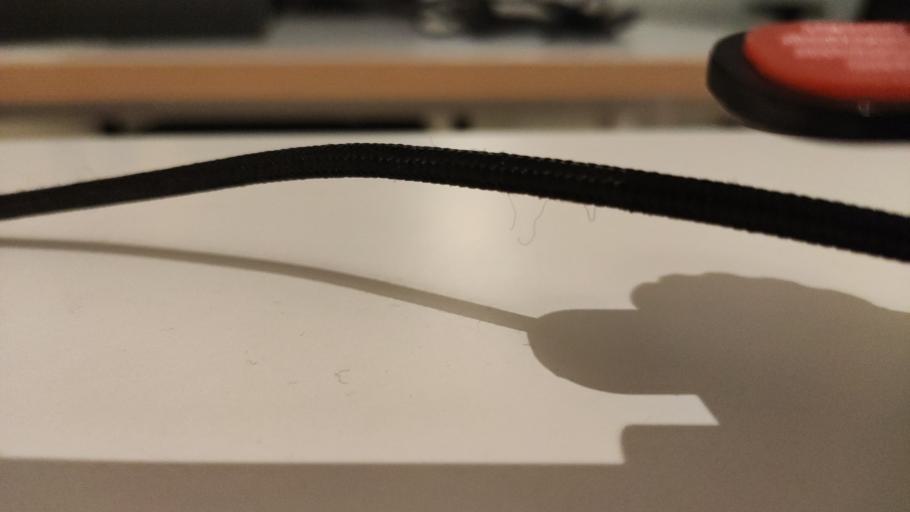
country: RU
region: Moskovskaya
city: Novoye
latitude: 55.6358
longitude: 38.9291
